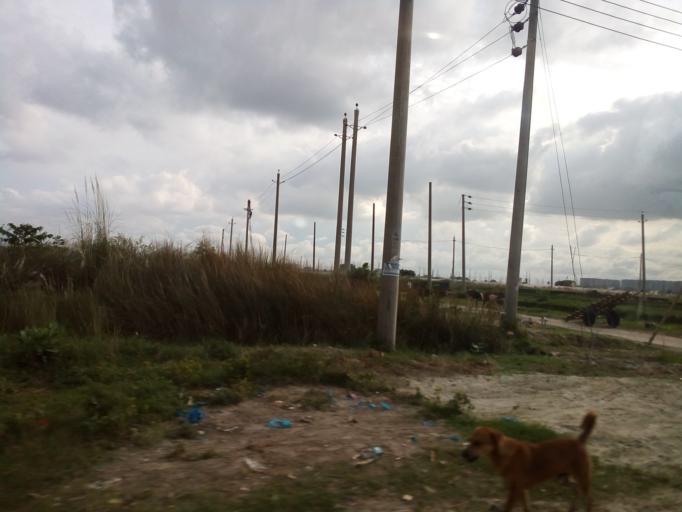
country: BD
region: Dhaka
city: Tungi
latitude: 23.8671
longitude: 90.3733
